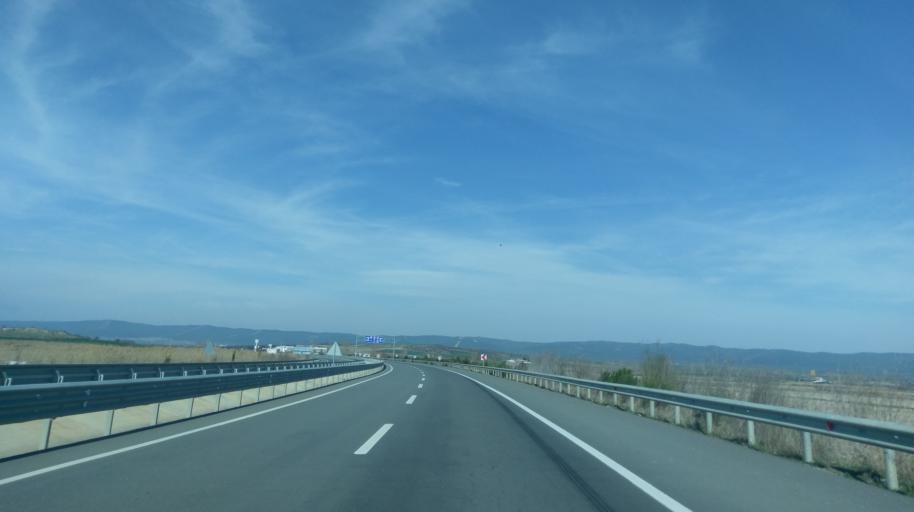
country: TR
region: Canakkale
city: Evrese
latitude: 40.6349
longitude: 26.8674
